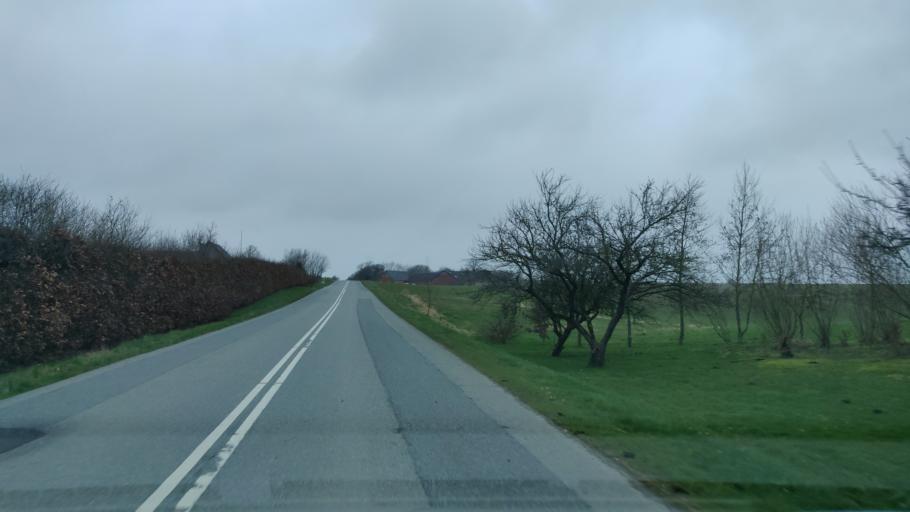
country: DK
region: Central Jutland
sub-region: Skive Kommune
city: Hojslev
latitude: 56.5861
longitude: 9.2247
